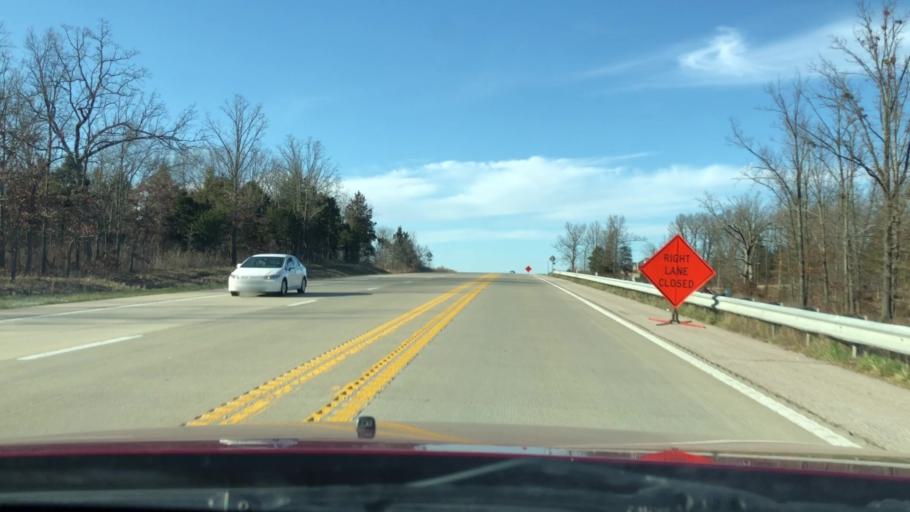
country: US
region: Missouri
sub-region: Camden County
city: Camdenton
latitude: 37.9458
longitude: -92.7157
